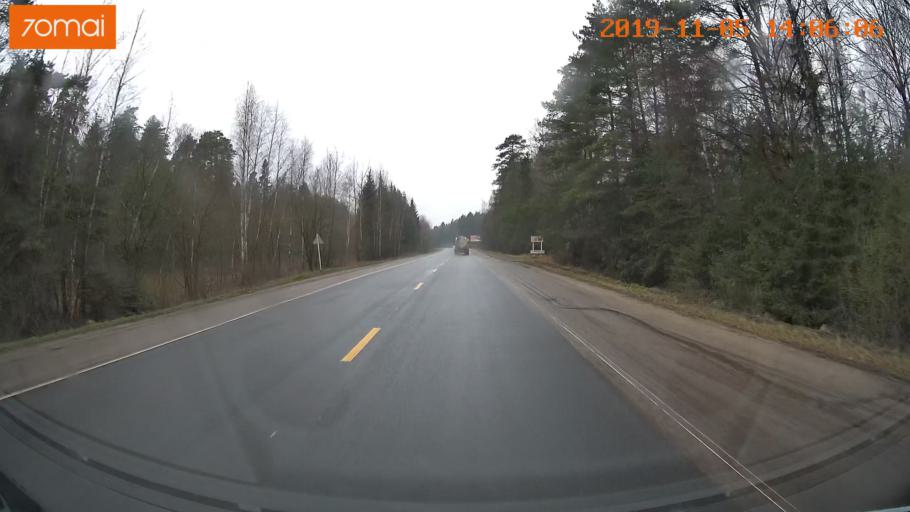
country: RU
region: Ivanovo
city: Kokhma
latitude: 56.9979
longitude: 41.1455
